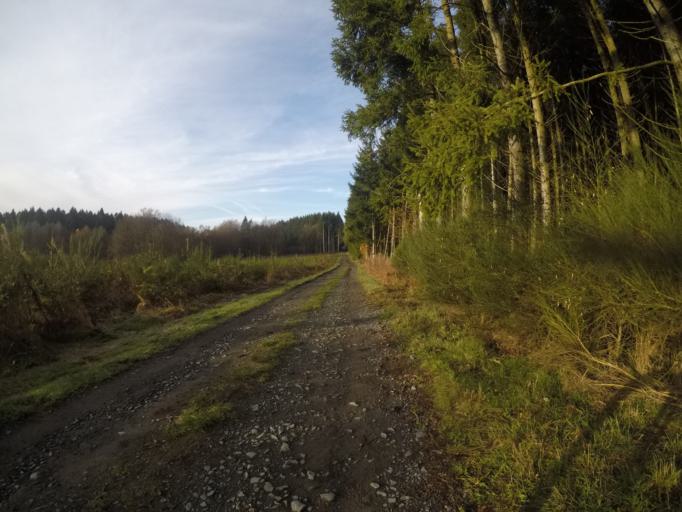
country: BE
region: Wallonia
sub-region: Province du Luxembourg
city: Habay-la-Vieille
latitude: 49.7737
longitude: 5.6370
